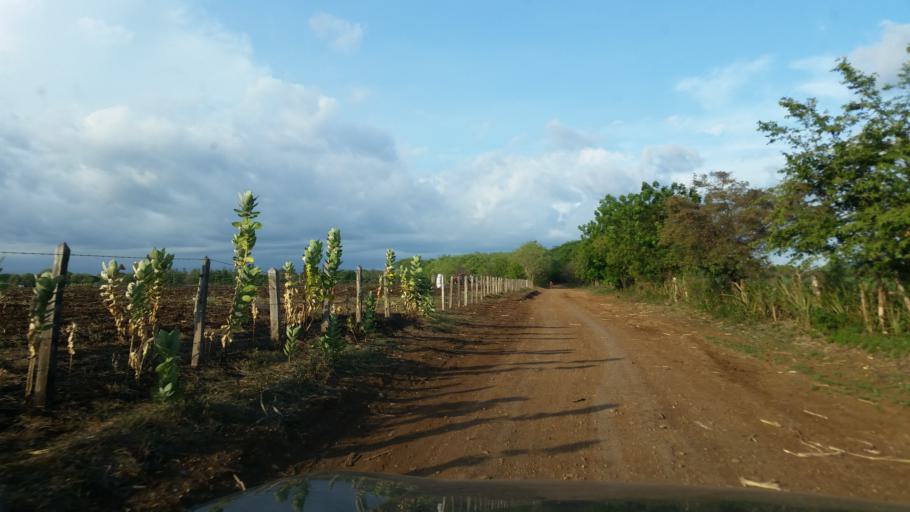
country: NI
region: Managua
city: Masachapa
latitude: 11.7758
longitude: -86.4830
